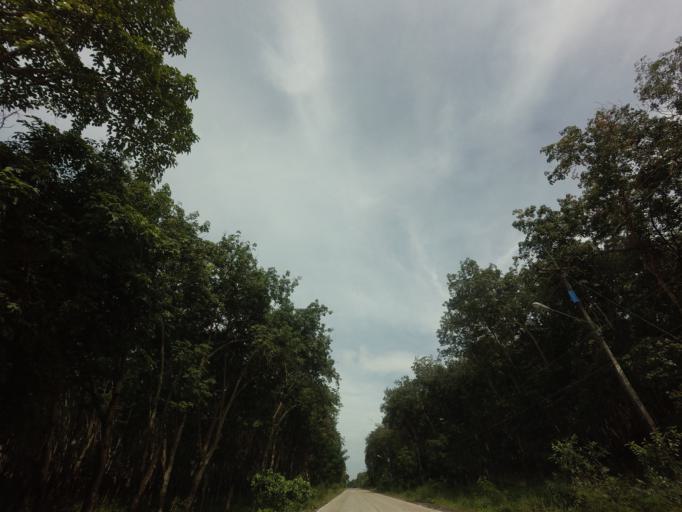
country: TH
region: Rayong
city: Klaeng
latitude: 12.6616
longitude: 101.5584
